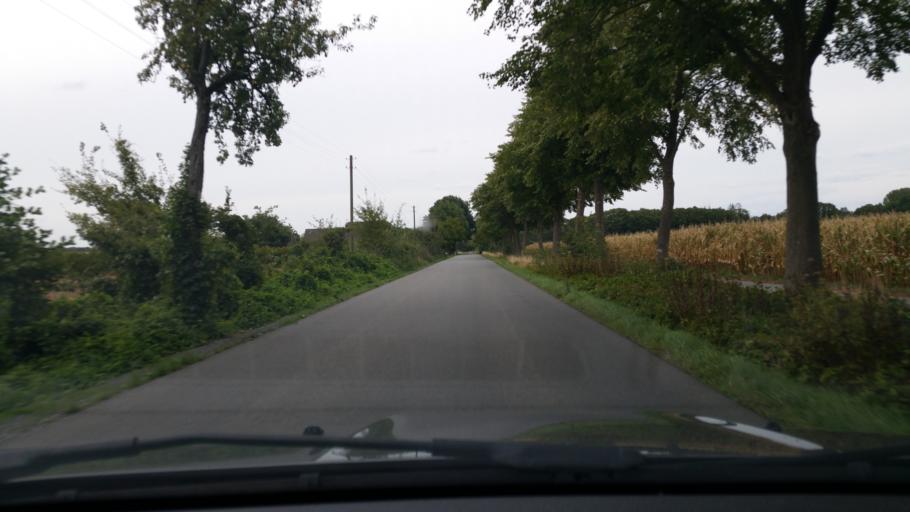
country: DE
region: North Rhine-Westphalia
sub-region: Regierungsbezirk Dusseldorf
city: Bocholt
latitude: 51.8616
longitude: 6.6370
